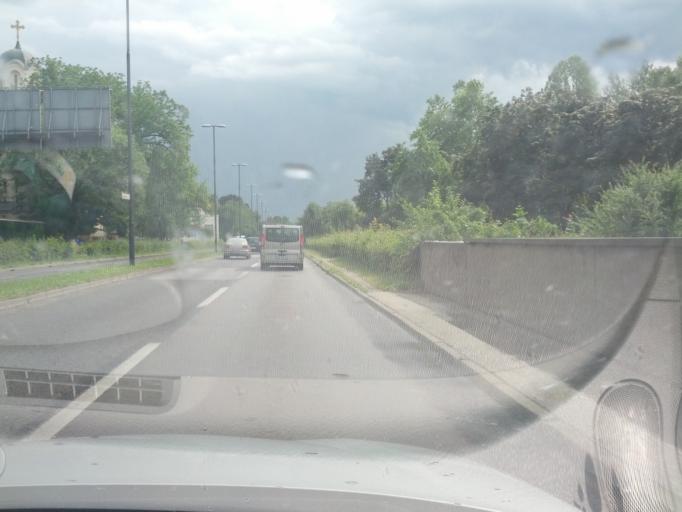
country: SI
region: Ljubljana
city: Ljubljana
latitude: 46.0550
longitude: 14.4997
